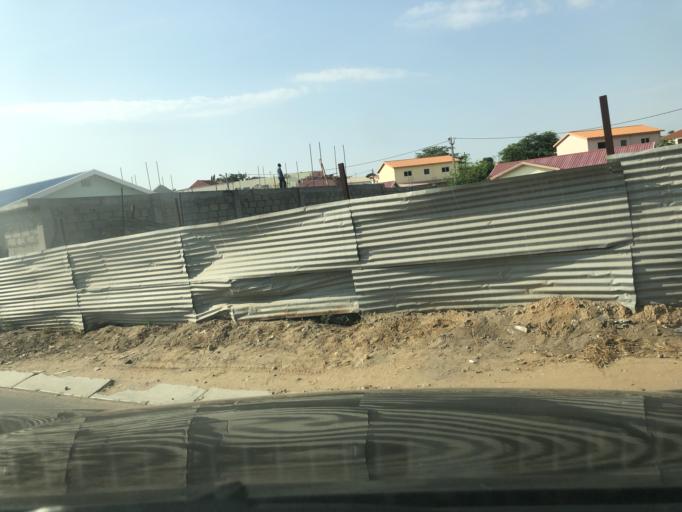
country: AO
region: Luanda
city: Luanda
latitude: -8.9108
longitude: 13.2263
